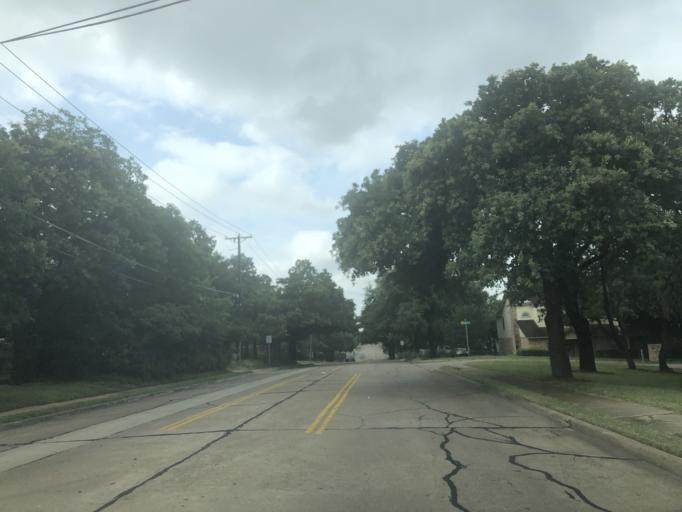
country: US
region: Texas
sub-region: Dallas County
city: Irving
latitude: 32.8061
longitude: -96.9631
